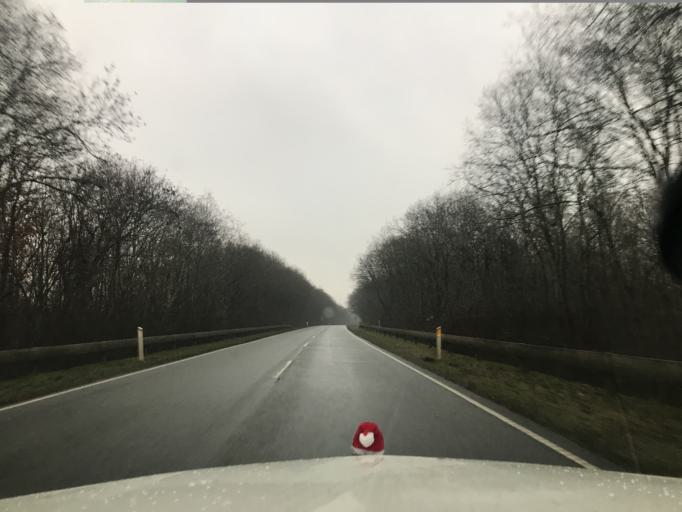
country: DK
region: South Denmark
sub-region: Aabenraa Kommune
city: Aabenraa
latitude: 55.0026
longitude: 9.4265
